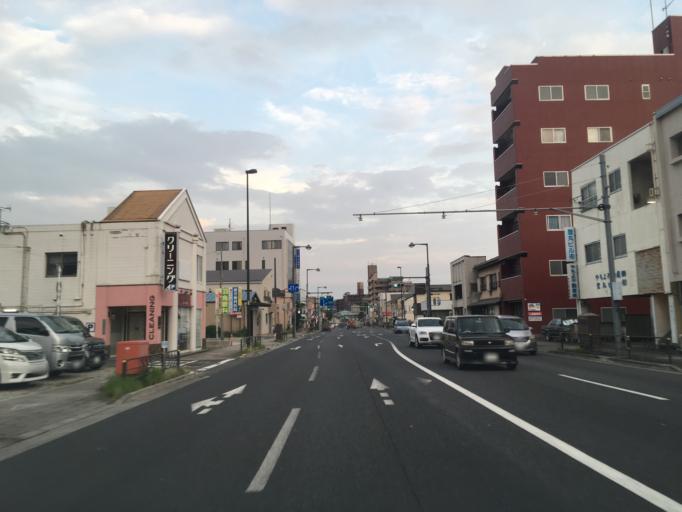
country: JP
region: Gunma
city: Maebashi-shi
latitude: 36.3871
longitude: 139.0749
